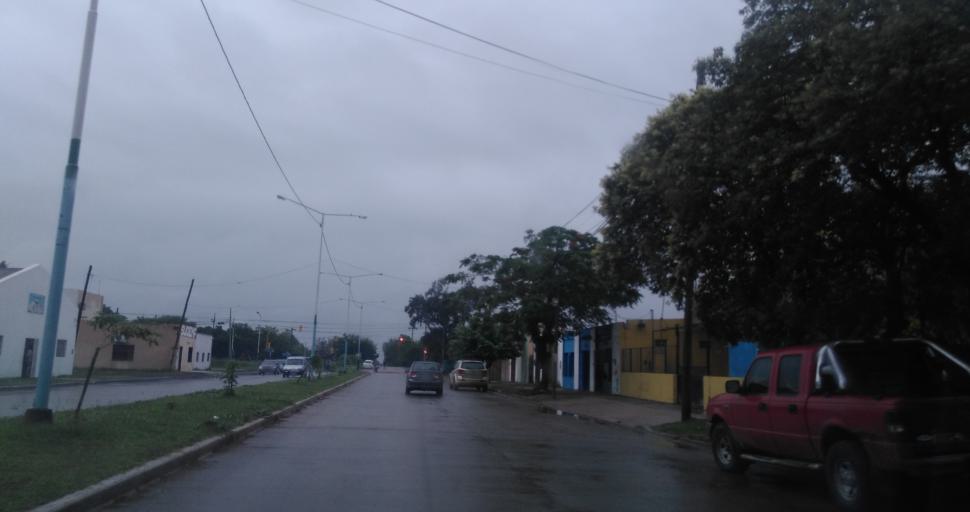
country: AR
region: Chaco
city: Fontana
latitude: -27.4176
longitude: -59.0368
